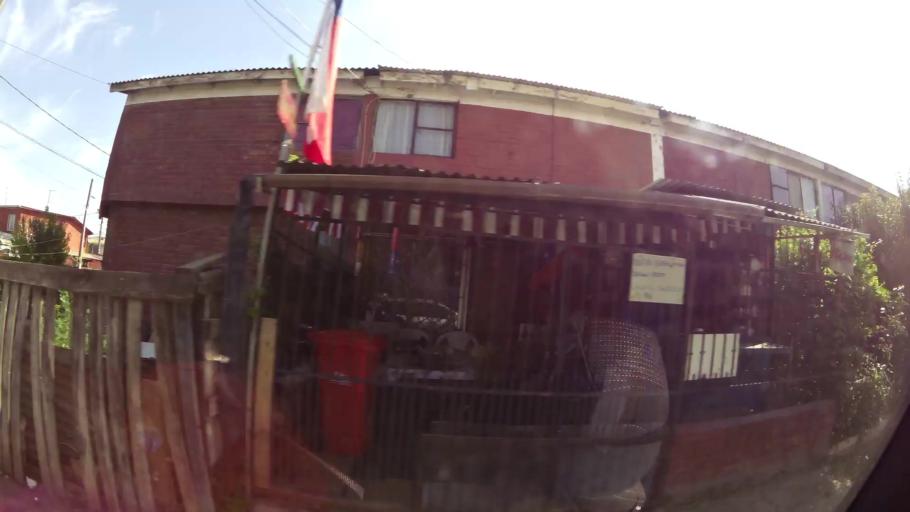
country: CL
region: Santiago Metropolitan
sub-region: Provincia de Talagante
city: Talagante
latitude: -33.6782
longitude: -70.9474
